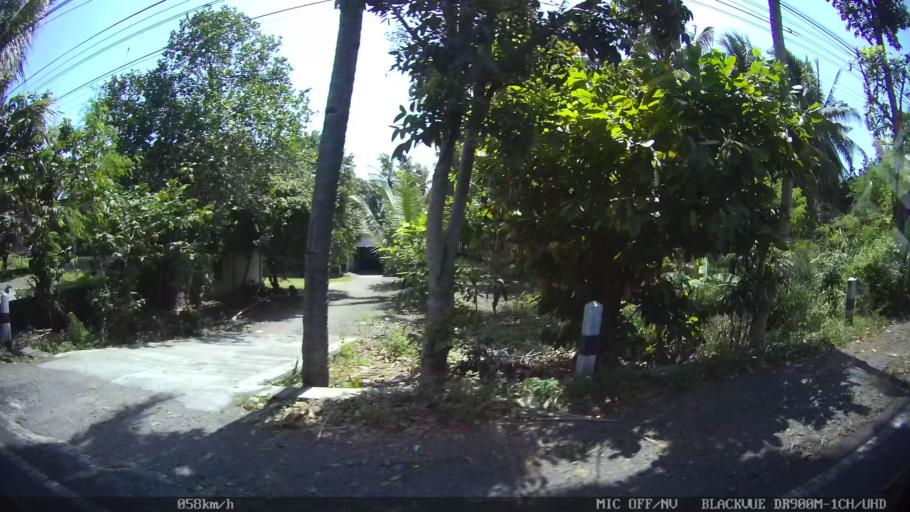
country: ID
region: Daerah Istimewa Yogyakarta
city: Srandakan
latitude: -7.9124
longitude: 110.0923
